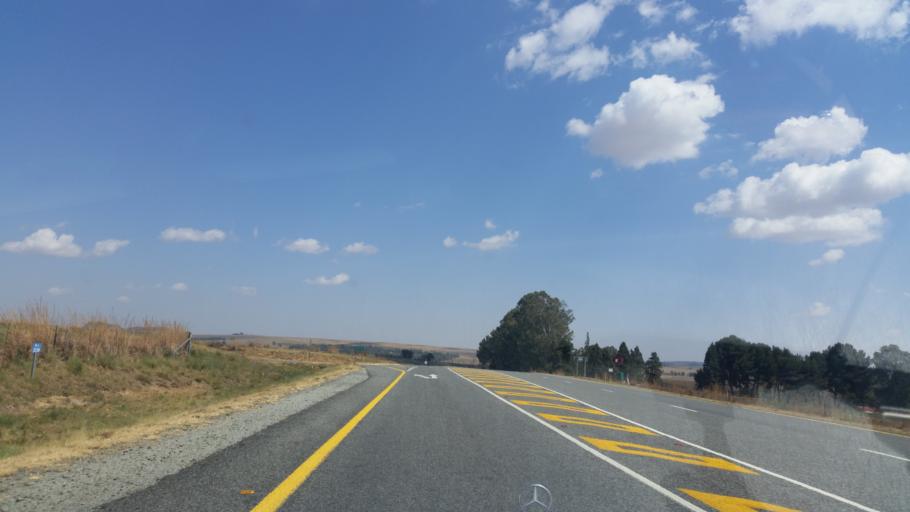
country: ZA
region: Orange Free State
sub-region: Thabo Mofutsanyana District Municipality
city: Bethlehem
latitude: -28.2738
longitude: 28.0967
